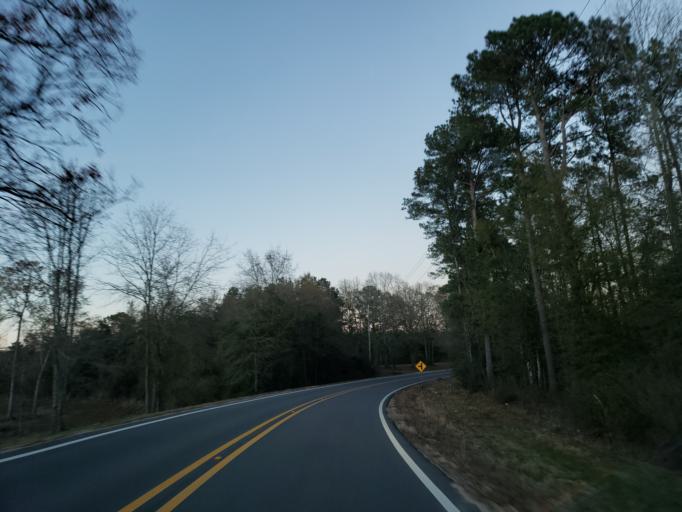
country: US
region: Mississippi
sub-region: Jones County
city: Ellisville
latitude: 31.5782
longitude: -89.2838
